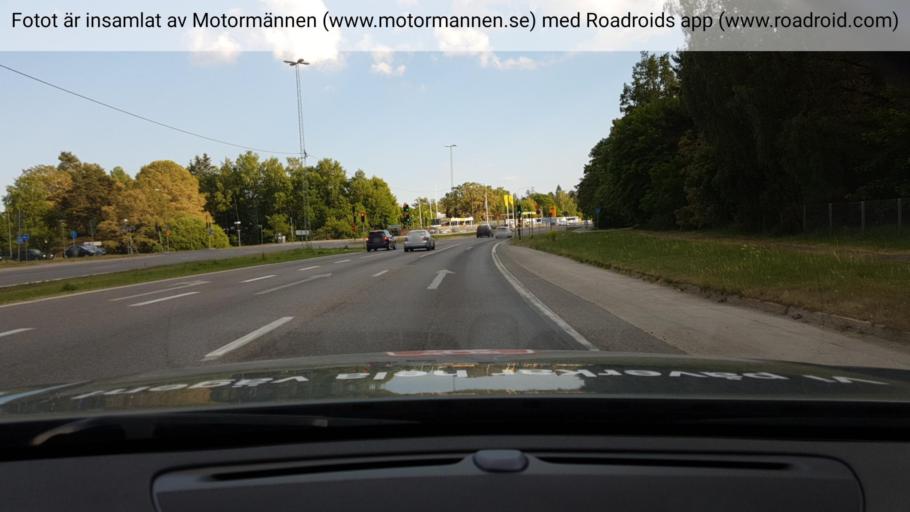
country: SE
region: Stockholm
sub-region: Huddinge Kommun
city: Huddinge
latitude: 59.2578
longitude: 18.0133
